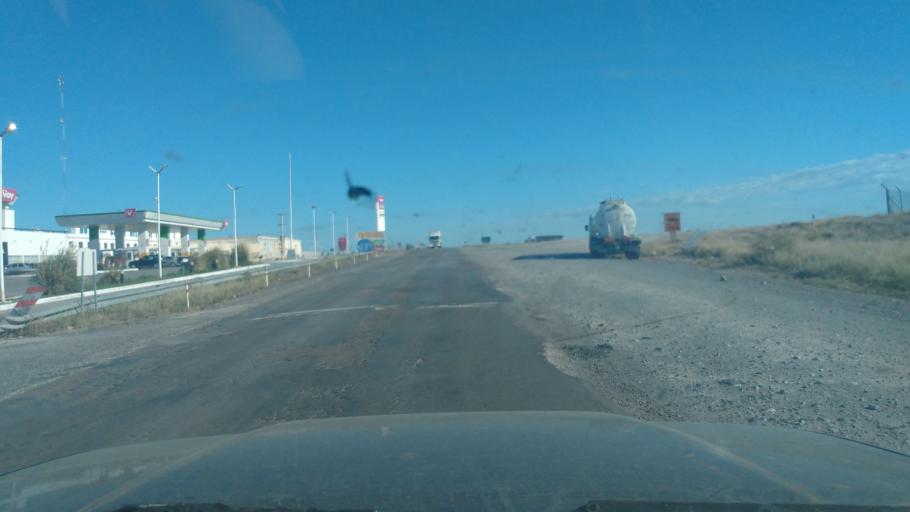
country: AR
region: La Pampa
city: Veinticinco de Mayo
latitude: -37.6624
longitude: -67.7489
